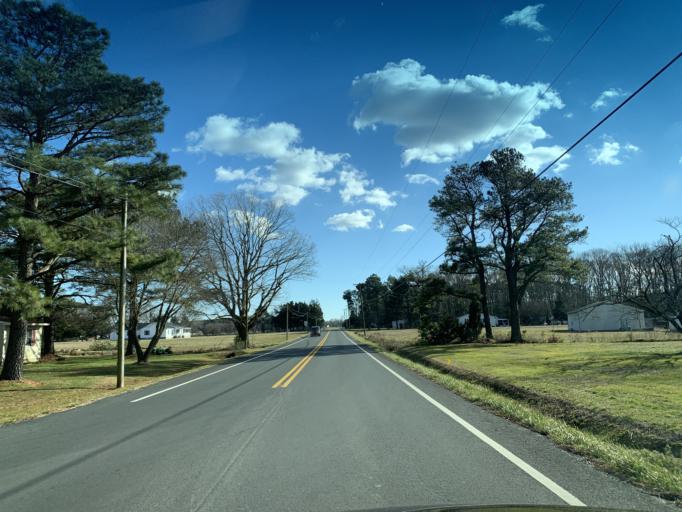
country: US
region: Maryland
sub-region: Worcester County
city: Berlin
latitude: 38.3558
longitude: -75.1966
